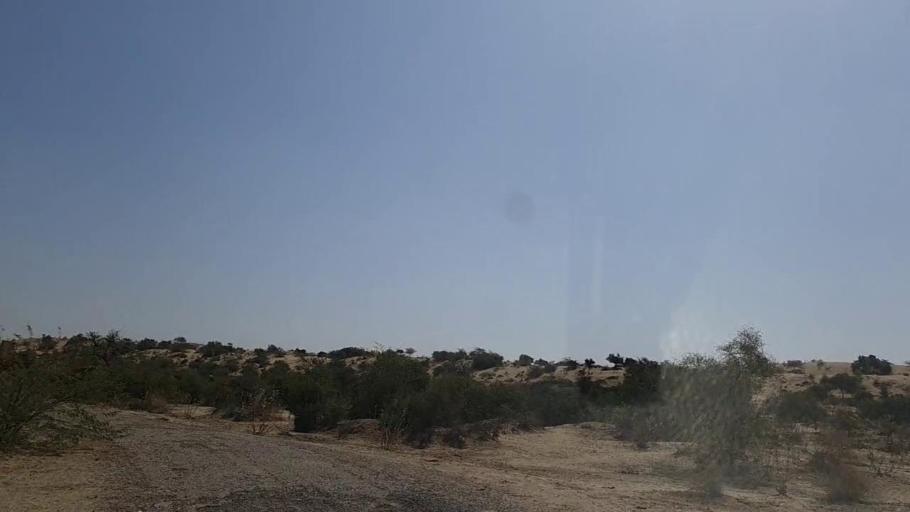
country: PK
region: Sindh
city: Mithi
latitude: 24.7032
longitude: 69.5929
